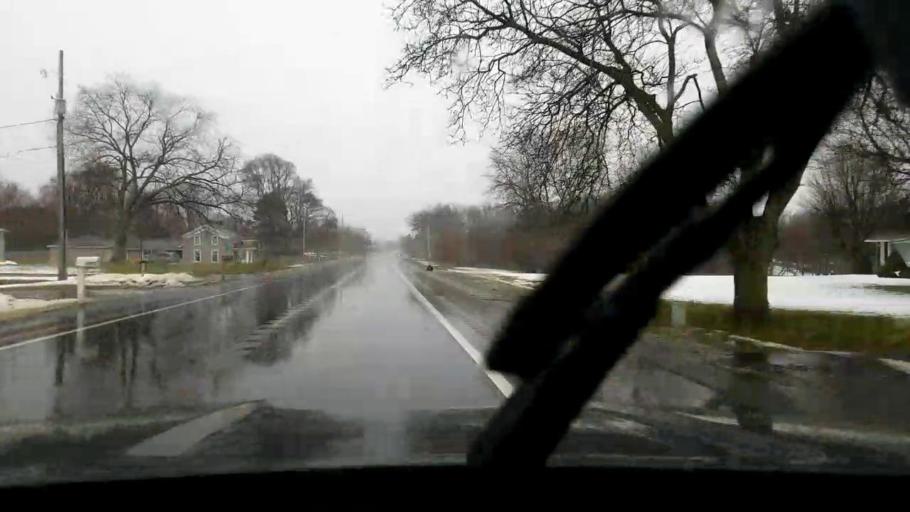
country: US
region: Michigan
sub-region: Jackson County
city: Michigan Center
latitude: 42.1910
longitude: -84.3162
